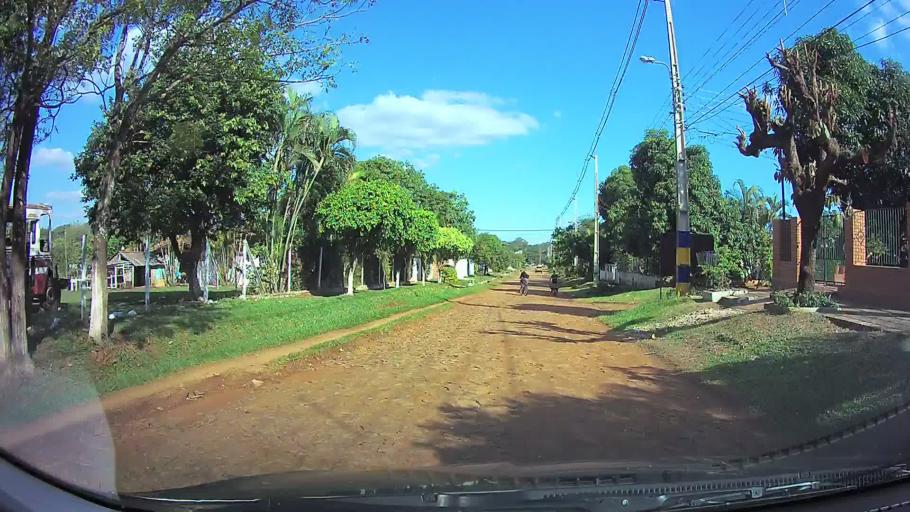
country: PY
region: Central
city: Limpio
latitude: -25.2533
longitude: -57.4749
